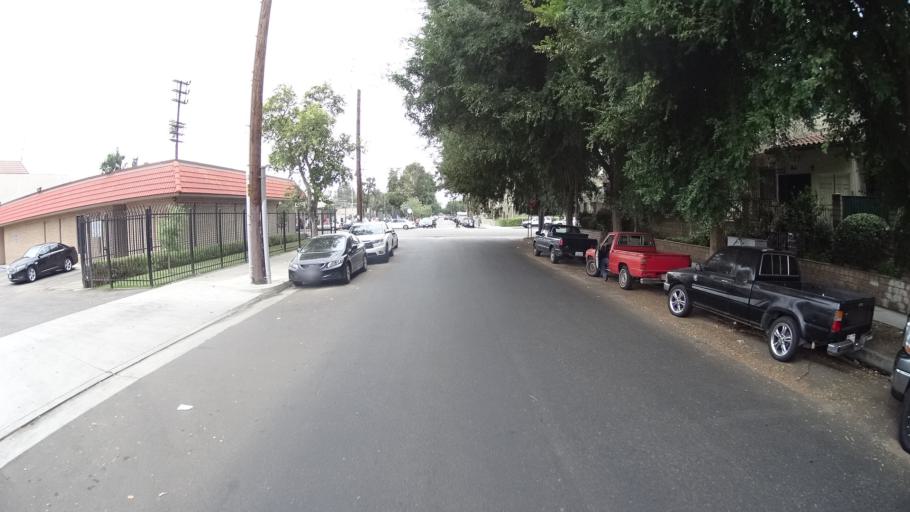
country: US
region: California
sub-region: Los Angeles County
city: San Fernando
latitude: 34.2359
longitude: -118.4517
